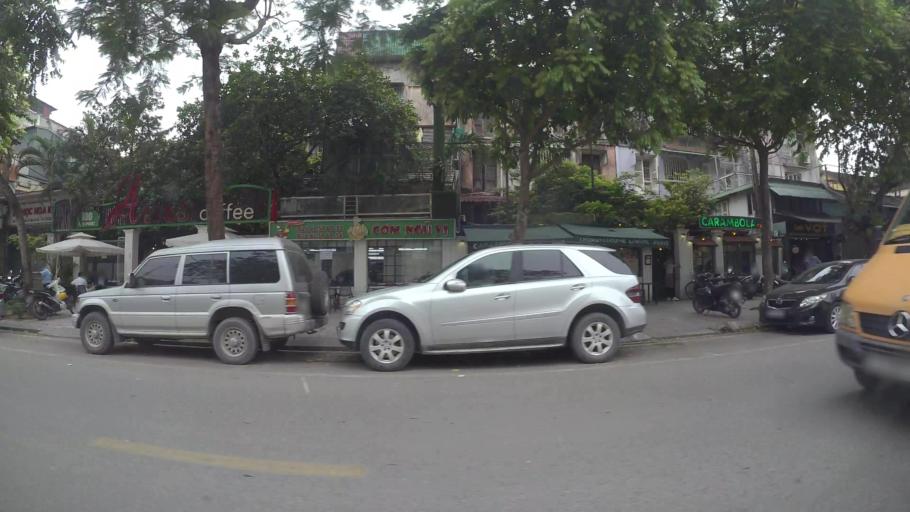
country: VN
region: Ha Noi
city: Cau Giay
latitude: 21.0335
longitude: 105.8161
